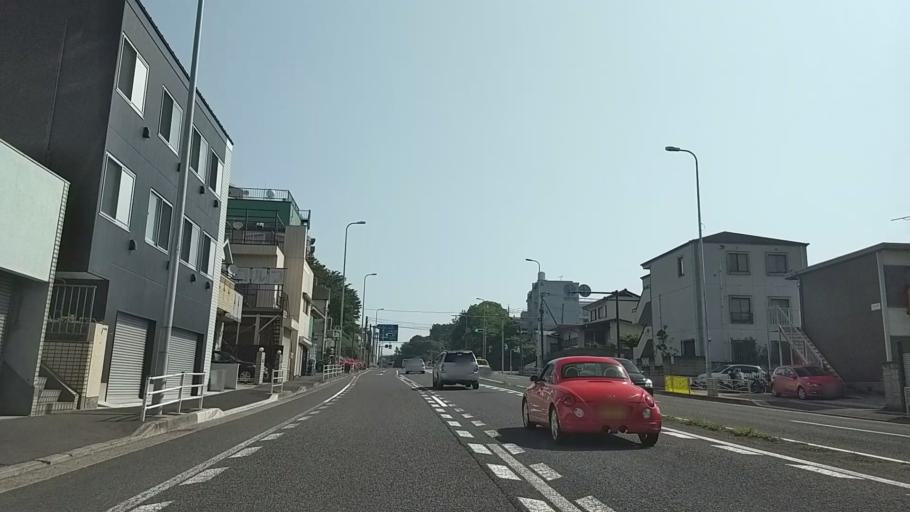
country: JP
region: Kanagawa
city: Yokohama
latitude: 35.4933
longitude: 139.6567
